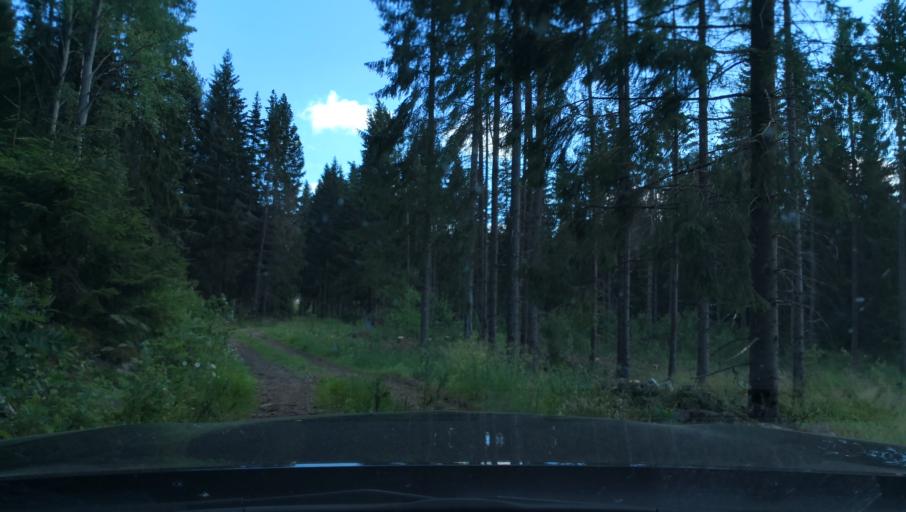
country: SE
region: Vaestmanland
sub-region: Kungsors Kommun
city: Kungsoer
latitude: 59.3395
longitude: 16.0627
